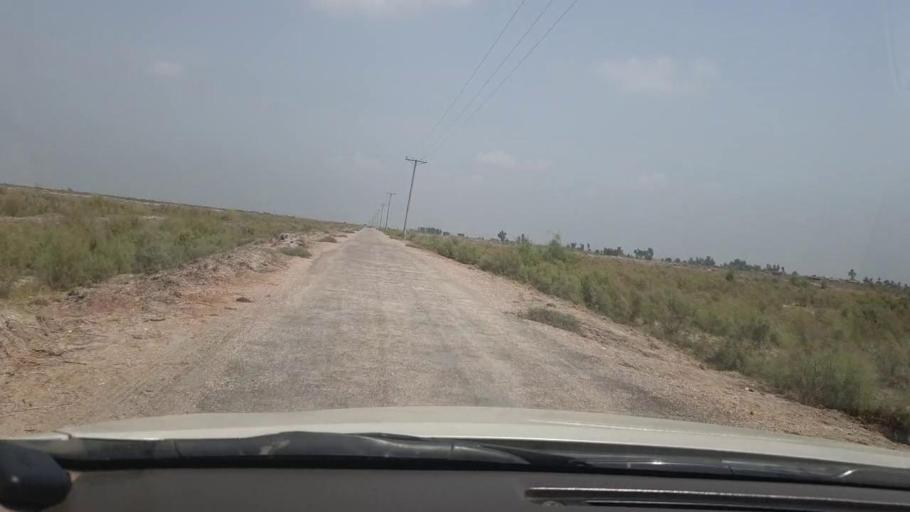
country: PK
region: Sindh
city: Garhi Yasin
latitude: 27.9908
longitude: 68.5014
